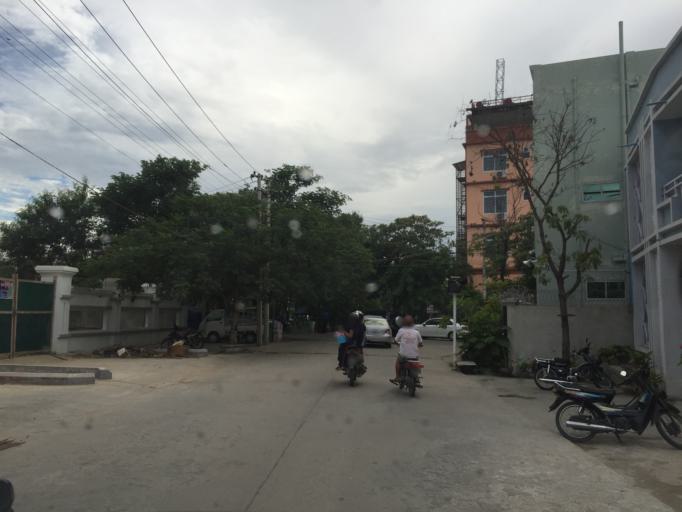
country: MM
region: Mandalay
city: Mandalay
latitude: 21.9705
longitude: 96.1073
